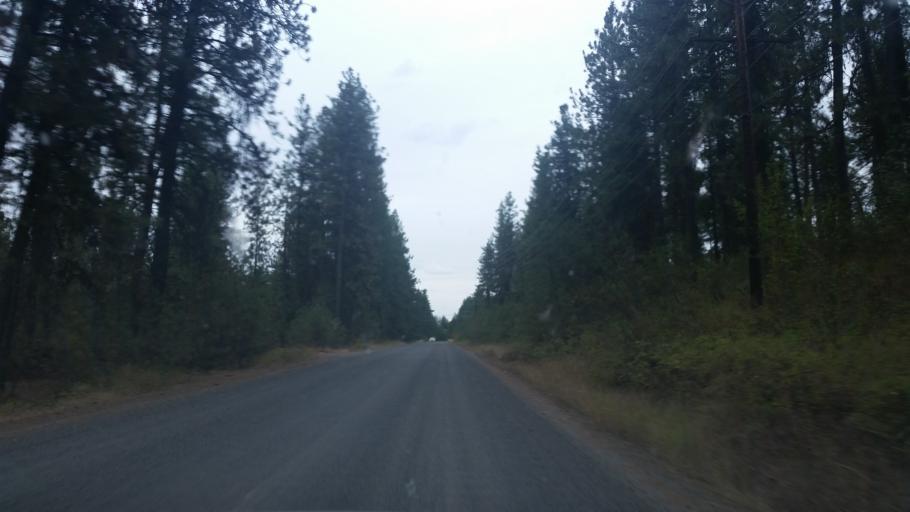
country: US
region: Washington
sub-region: Spokane County
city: Cheney
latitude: 47.5318
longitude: -117.5826
